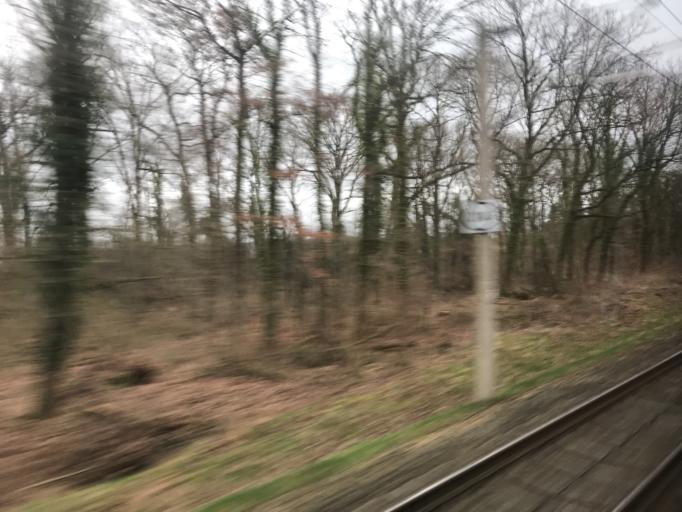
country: DE
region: Lower Saxony
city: Edemissen
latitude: 52.4416
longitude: 10.2810
